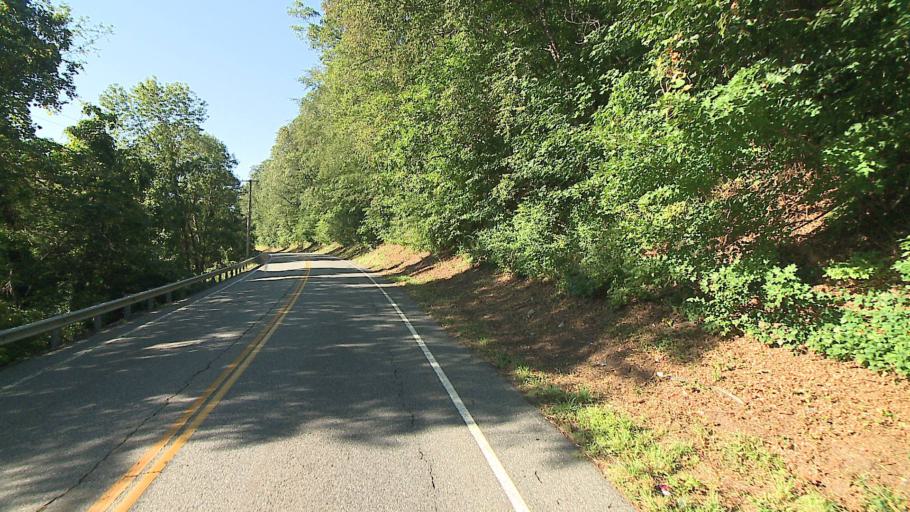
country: US
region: Connecticut
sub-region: New London County
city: Lisbon
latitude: 41.5691
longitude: -72.0125
